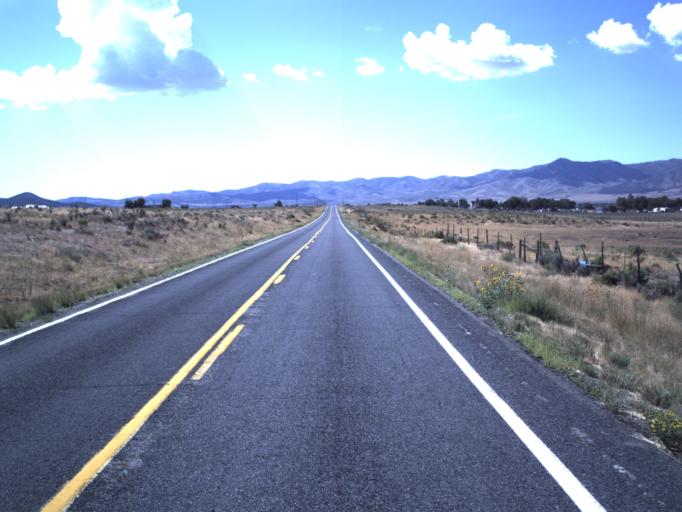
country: US
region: Utah
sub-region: Tooele County
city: Tooele
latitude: 40.1081
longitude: -112.4308
